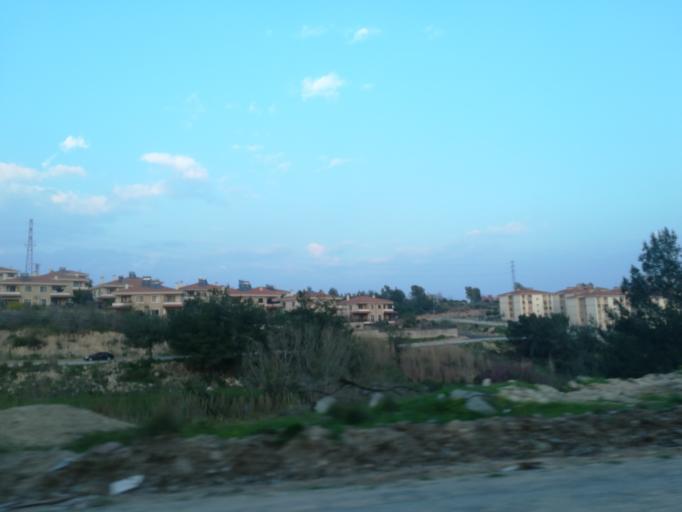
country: TR
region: Adana
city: Adana
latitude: 37.0814
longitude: 35.4094
